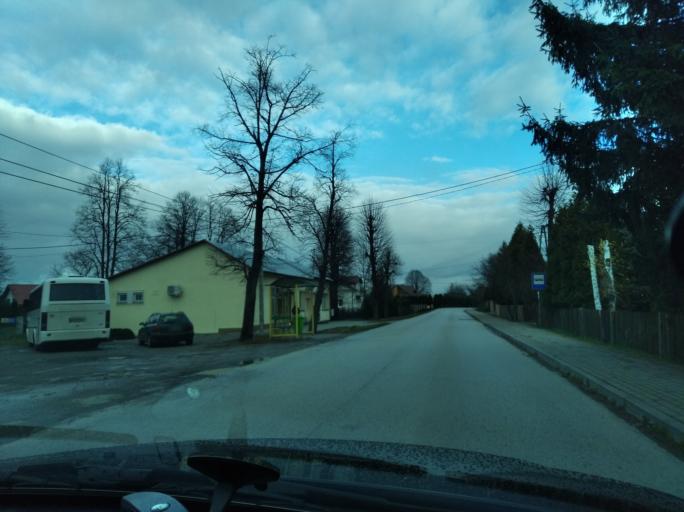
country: PL
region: Subcarpathian Voivodeship
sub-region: Powiat lancucki
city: Gluchow
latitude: 50.0980
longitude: 22.2629
